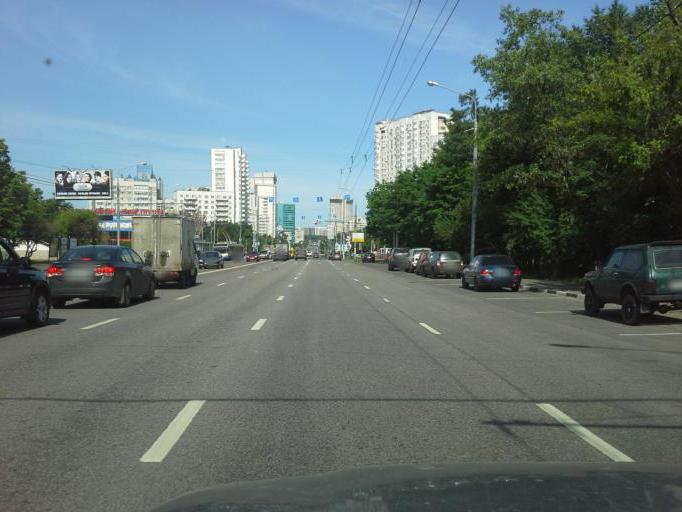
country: RU
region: Moscow
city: Zyuzino
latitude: 55.6558
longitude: 37.5737
